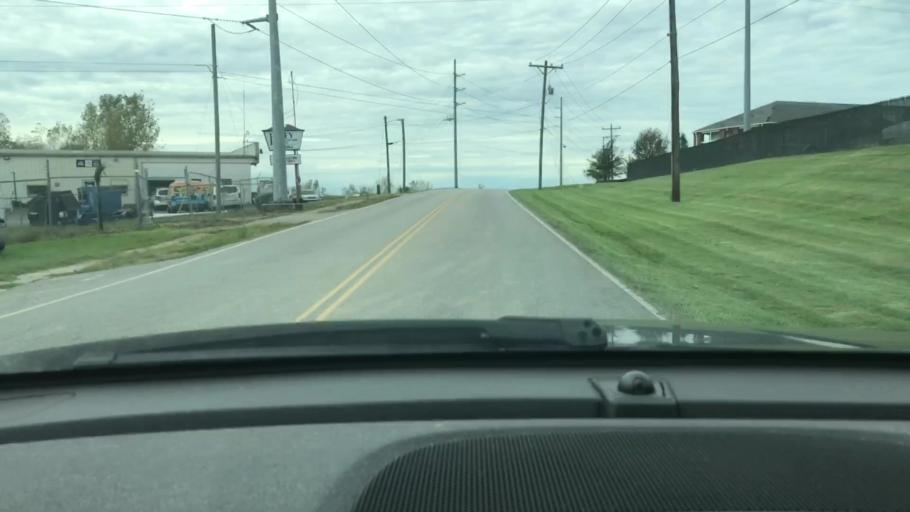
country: US
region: Tennessee
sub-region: Sumner County
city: Hendersonville
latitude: 36.3037
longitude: -86.6522
